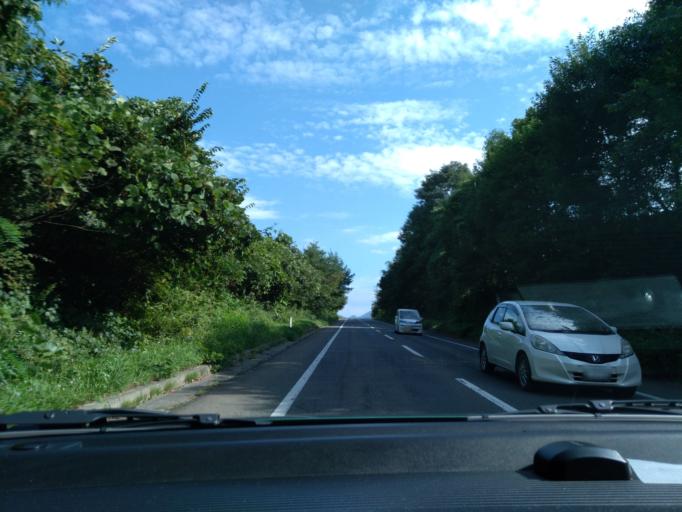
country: JP
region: Iwate
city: Shizukuishi
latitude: 39.6621
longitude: 140.9860
